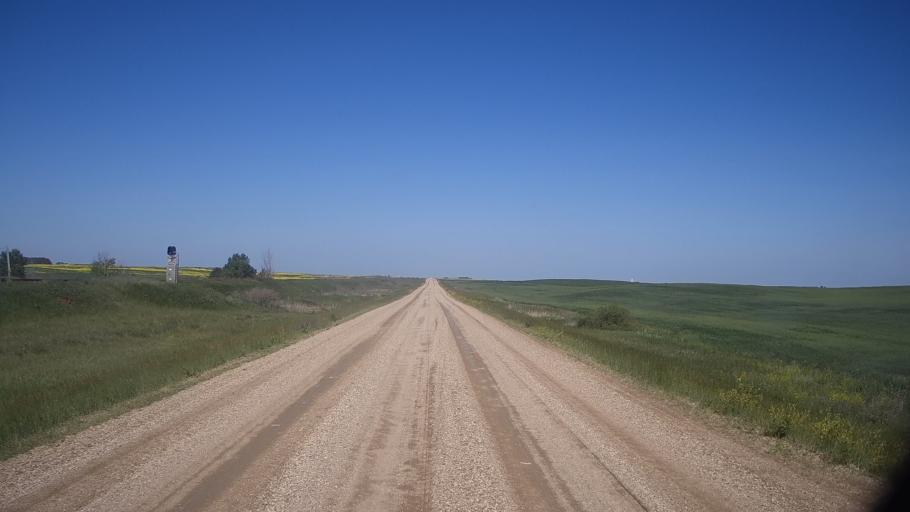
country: CA
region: Saskatchewan
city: Watrous
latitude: 51.8493
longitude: -105.9309
